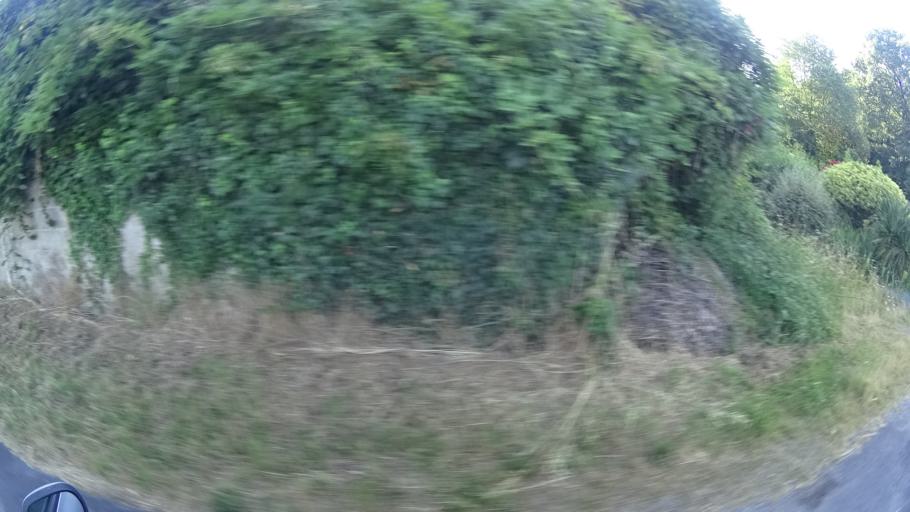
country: FR
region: Brittany
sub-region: Departement du Morbihan
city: Saint-Jean-la-Poterie
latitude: 47.6331
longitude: -2.1055
